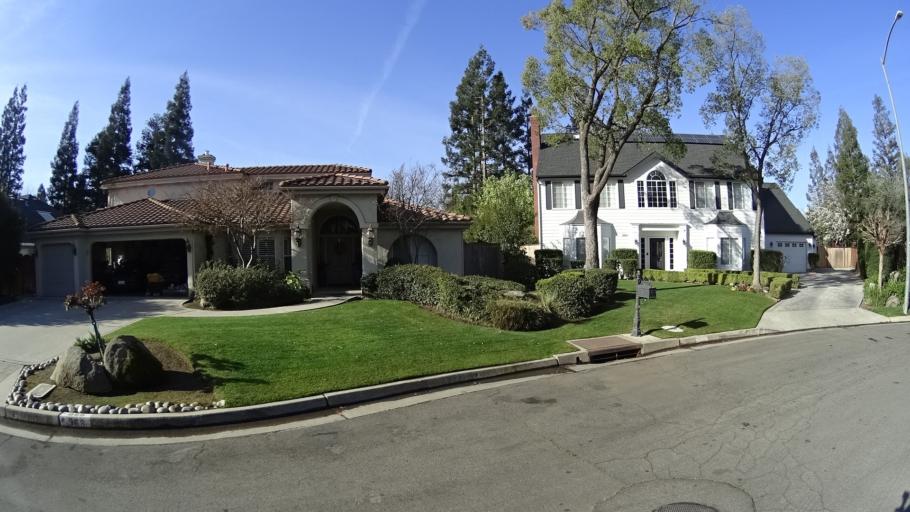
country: US
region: California
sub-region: Fresno County
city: Clovis
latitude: 36.8770
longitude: -119.7686
